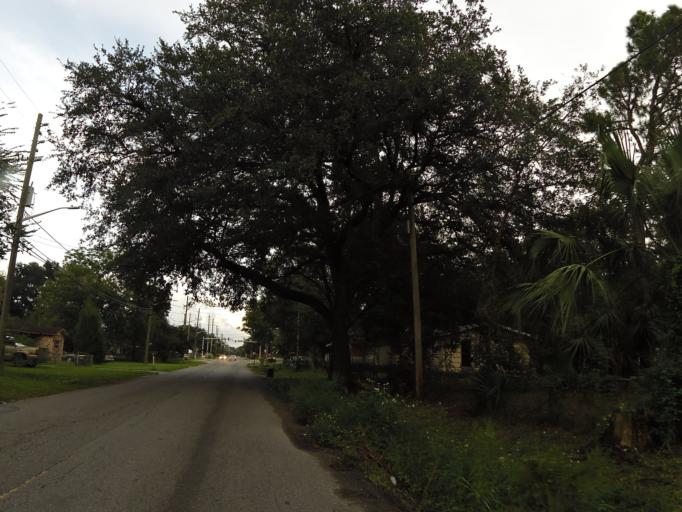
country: US
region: Florida
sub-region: Duval County
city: Jacksonville
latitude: 30.3438
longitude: -81.7159
